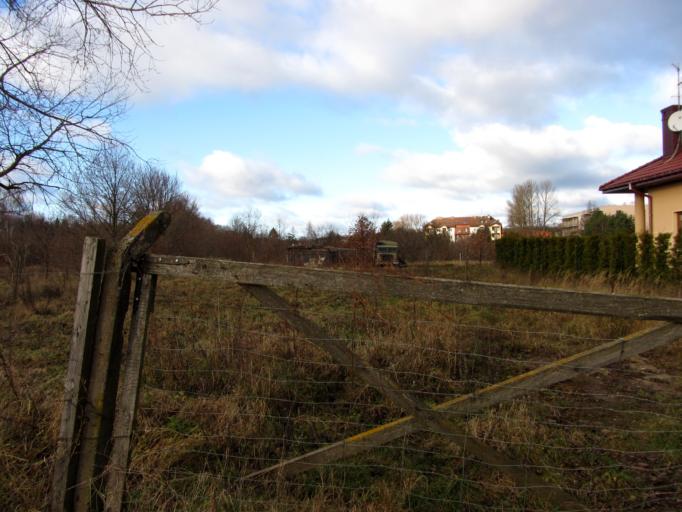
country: PL
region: West Pomeranian Voivodeship
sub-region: Powiat kolobrzeski
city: Kolobrzeg
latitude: 54.1728
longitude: 15.5469
